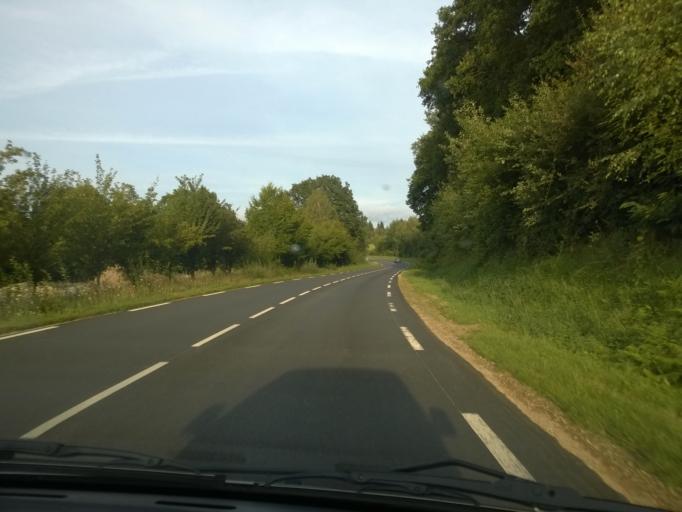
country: FR
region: Limousin
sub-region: Departement de la Haute-Vienne
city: Eymoutiers
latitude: 45.7358
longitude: 1.6845
